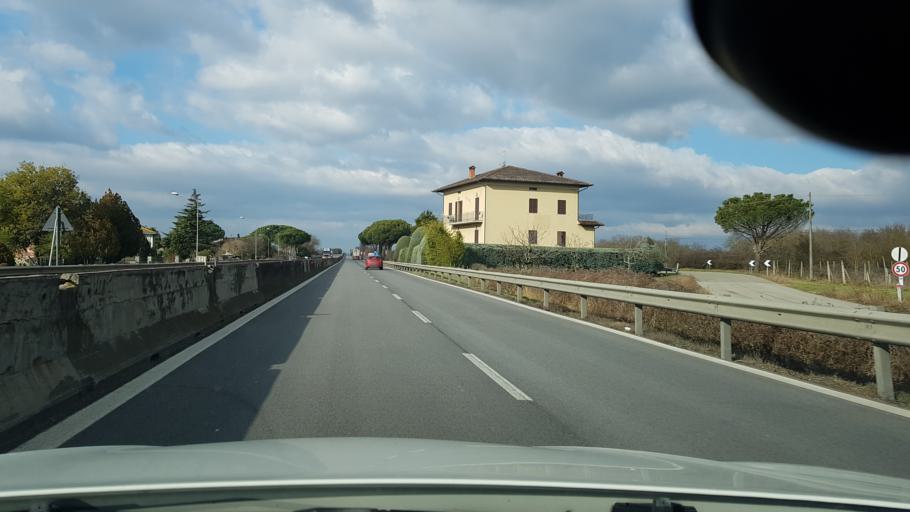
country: IT
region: Tuscany
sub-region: Province of Arezzo
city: Terontola
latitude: 43.1869
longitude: 12.0310
